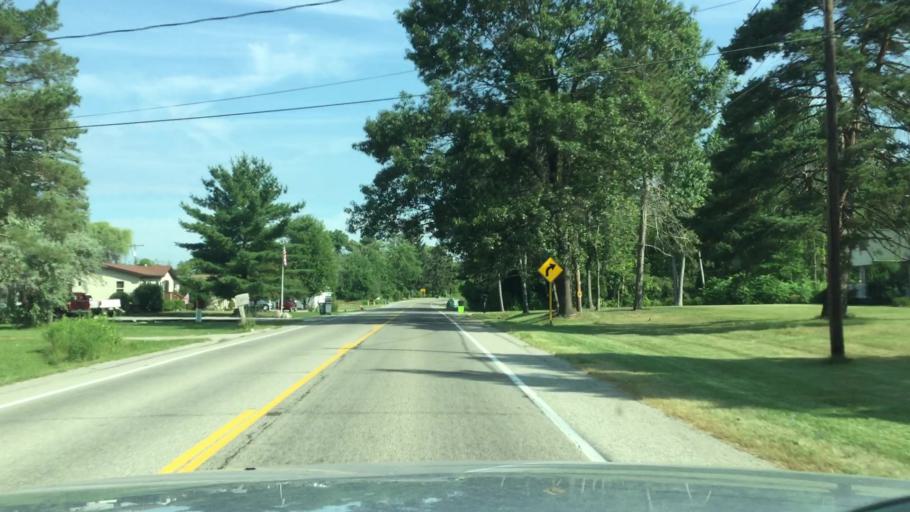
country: US
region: Michigan
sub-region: Genesee County
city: Flushing
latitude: 43.1057
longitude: -83.8714
